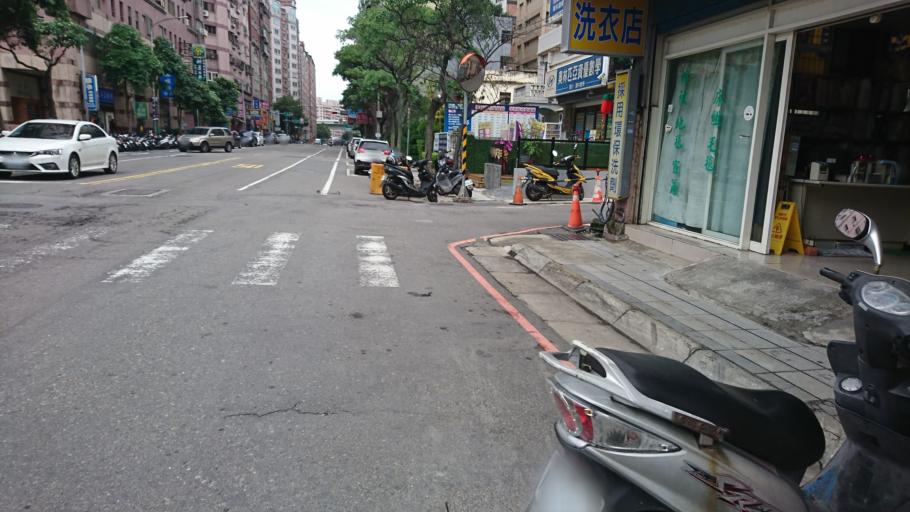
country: TW
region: Taiwan
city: Taoyuan City
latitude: 25.0550
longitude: 121.2989
